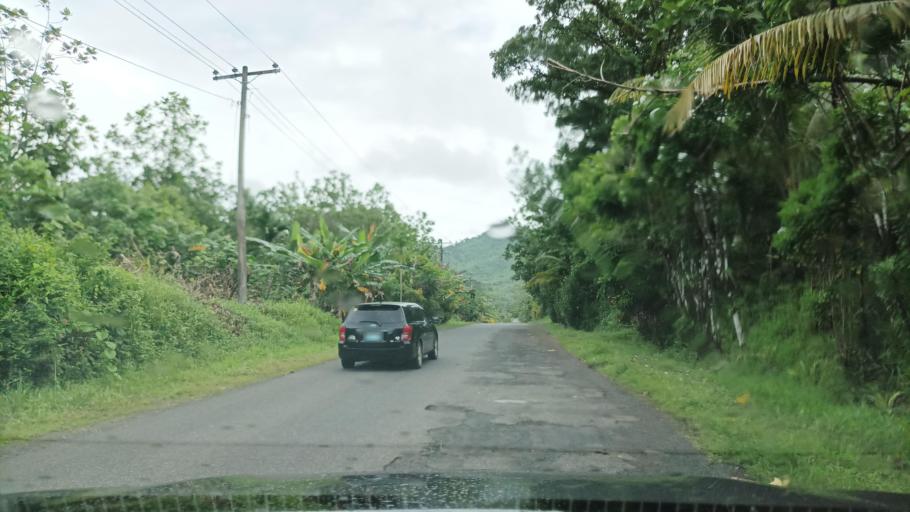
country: FM
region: Pohnpei
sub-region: Madolenihm Municipality
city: Madolenihm Municipality Government
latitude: 6.9219
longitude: 158.2875
